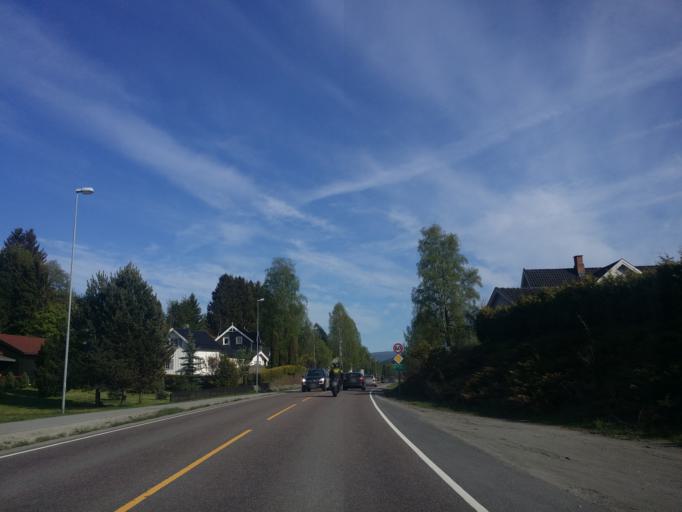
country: NO
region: Telemark
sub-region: Notodden
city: Notodden
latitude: 59.5749
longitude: 9.1954
